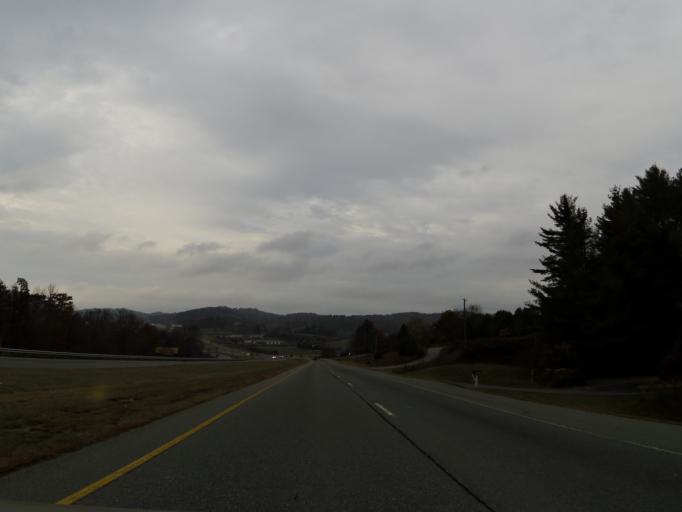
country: US
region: North Carolina
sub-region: Watauga County
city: Boone
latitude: 36.2337
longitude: -81.5051
